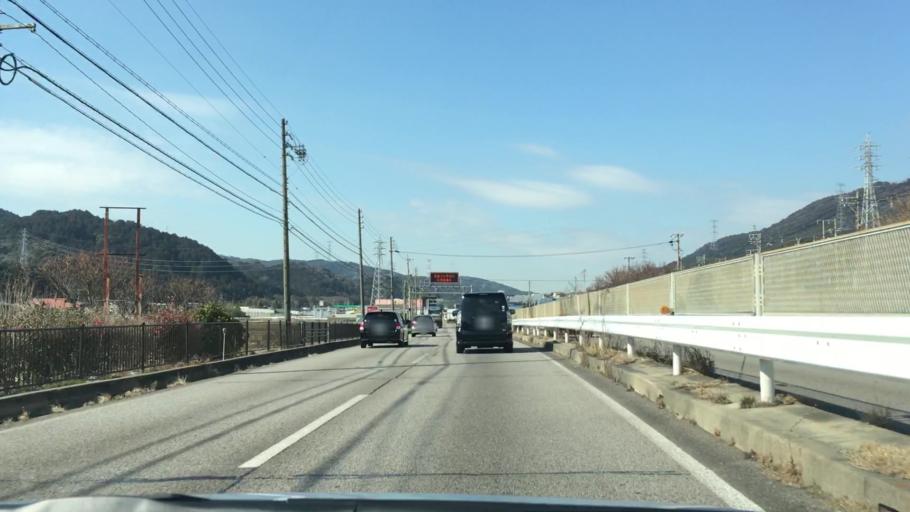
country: JP
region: Aichi
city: Gamagori
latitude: 34.8654
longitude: 137.3000
